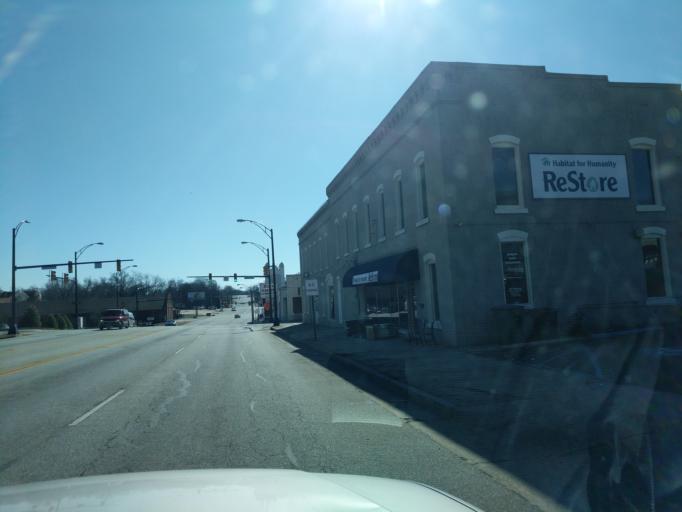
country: US
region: South Carolina
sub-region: Anderson County
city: Anderson
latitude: 34.5053
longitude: -82.6523
